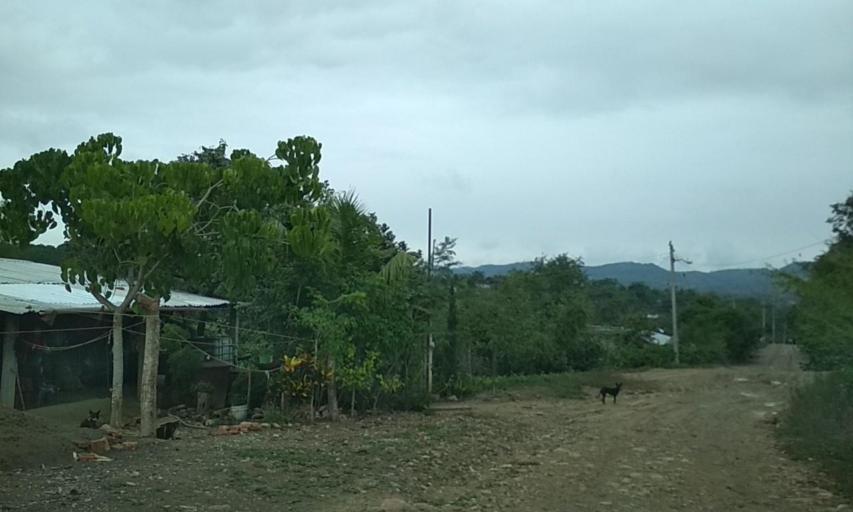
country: MX
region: Veracruz
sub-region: Papantla
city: El Chote
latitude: 20.3820
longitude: -97.3570
